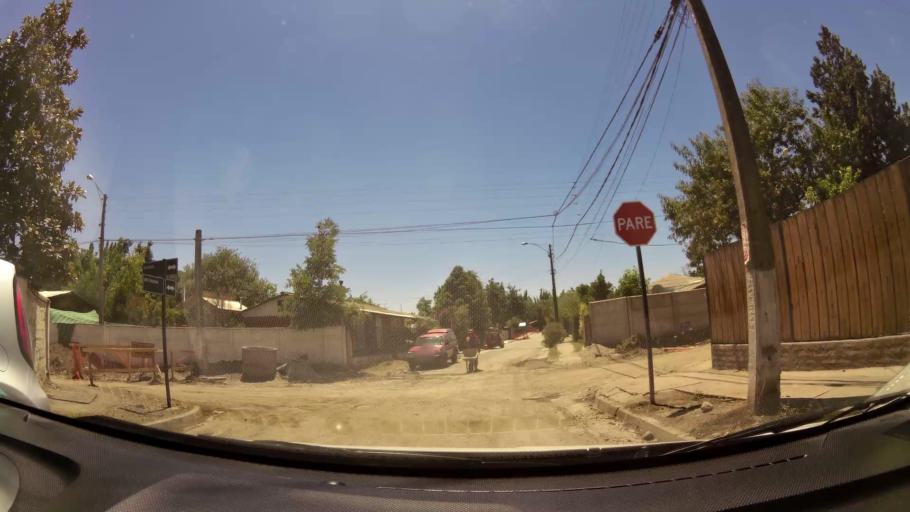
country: CL
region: O'Higgins
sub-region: Provincia de Cachapoal
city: Rancagua
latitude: -34.2229
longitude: -70.7849
